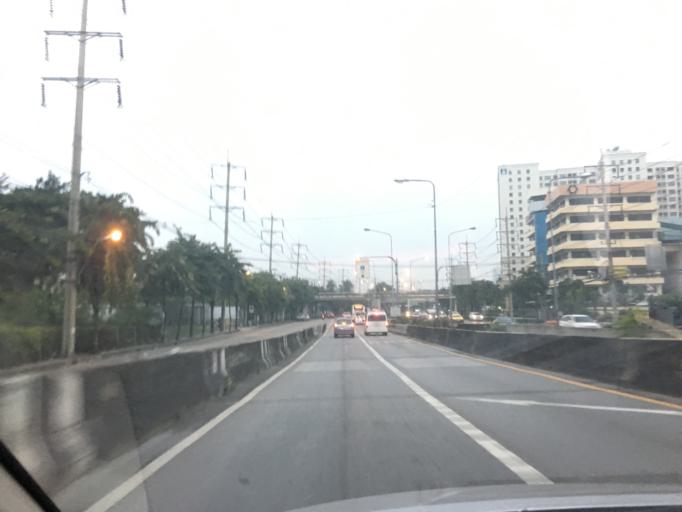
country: TH
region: Bangkok
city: Bang Kho Laem
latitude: 13.6897
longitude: 100.5072
